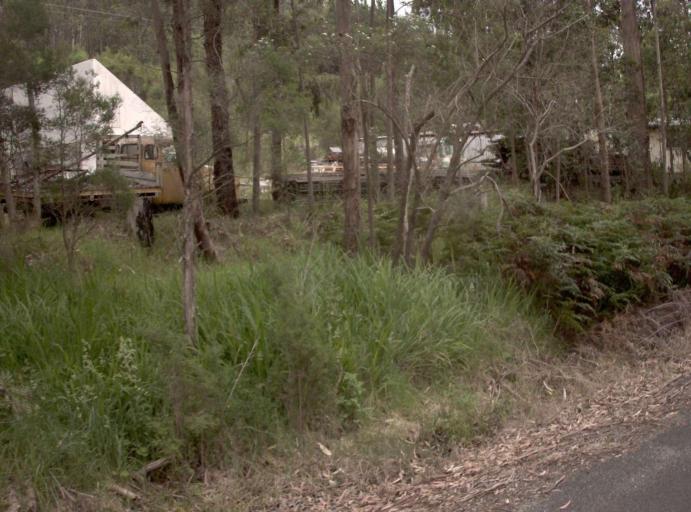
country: AU
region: New South Wales
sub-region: Bombala
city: Bombala
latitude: -37.4307
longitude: 149.1979
